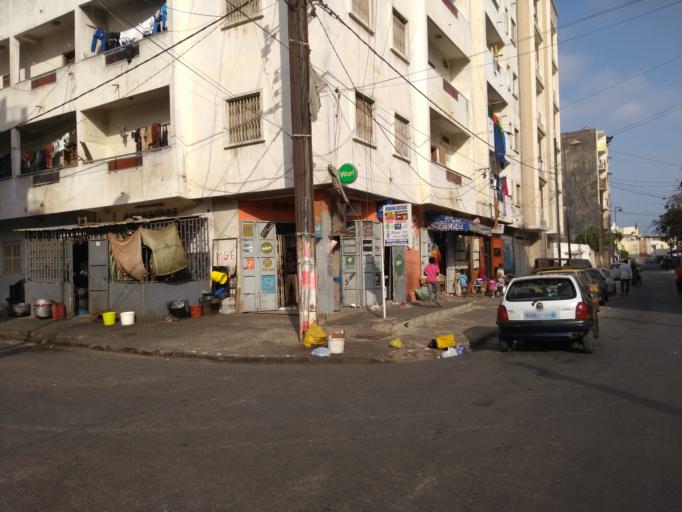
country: SN
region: Dakar
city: Dakar
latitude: 14.6868
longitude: -17.4471
